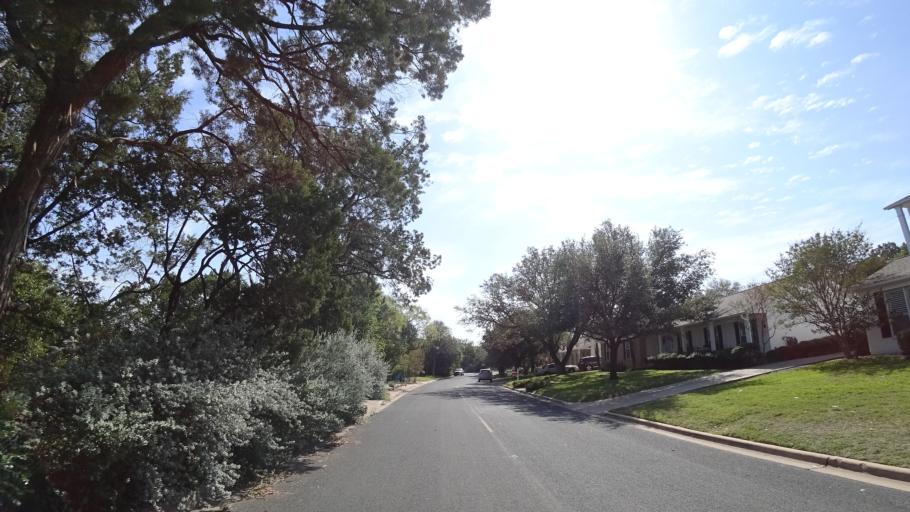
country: US
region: Texas
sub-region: Travis County
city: West Lake Hills
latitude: 30.3505
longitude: -97.7612
